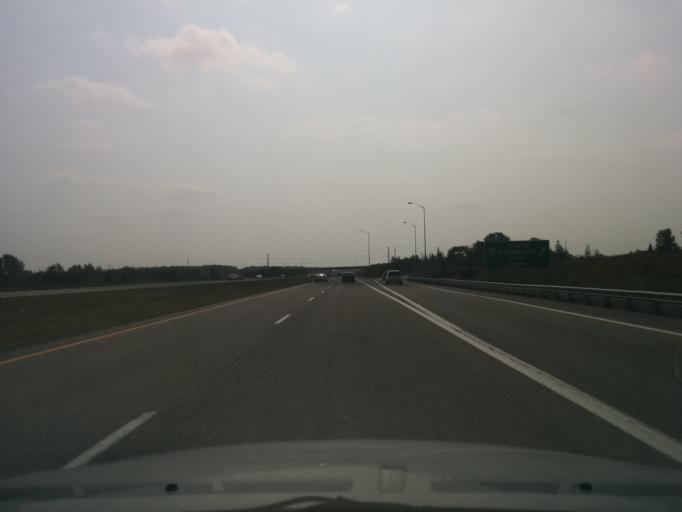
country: CA
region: Ontario
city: Bells Corners
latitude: 45.2751
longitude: -75.7997
